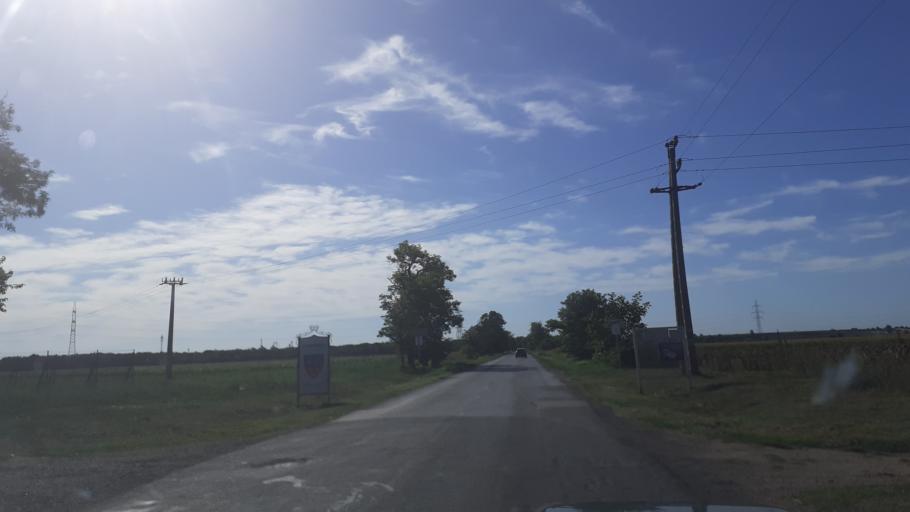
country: HU
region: Fejer
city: Ivancsa
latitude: 47.1854
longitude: 18.8003
